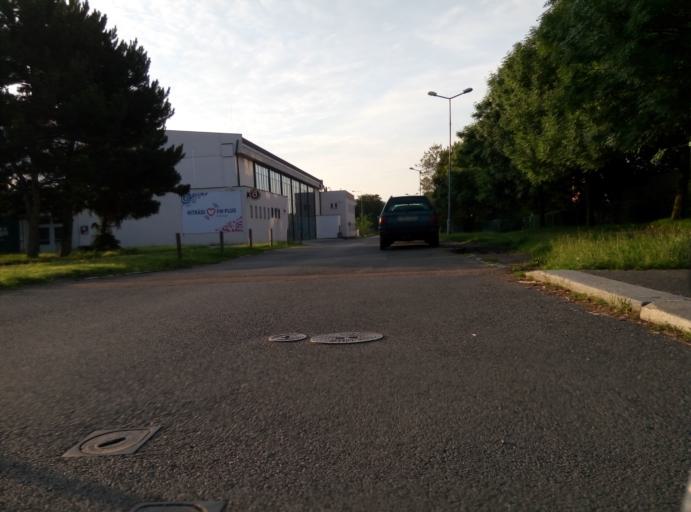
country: CZ
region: Plzensky
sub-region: Okres Plzen-Mesto
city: Pilsen
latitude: 49.7393
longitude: 13.3957
